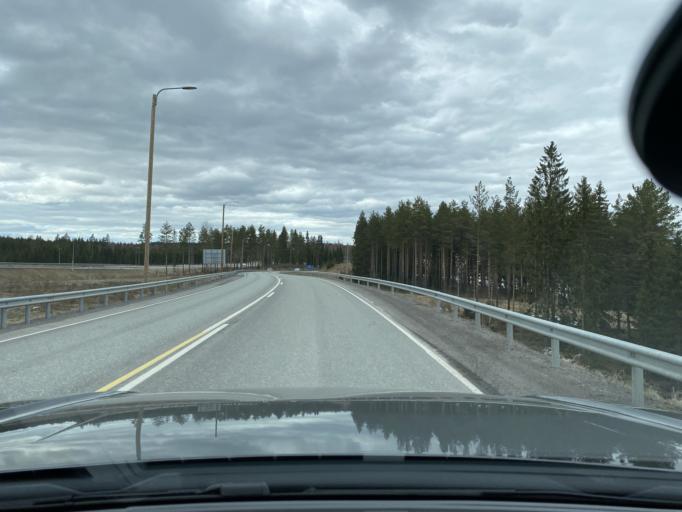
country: FI
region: Haeme
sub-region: Riihimaeki
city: Riihimaeki
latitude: 60.6889
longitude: 24.7528
